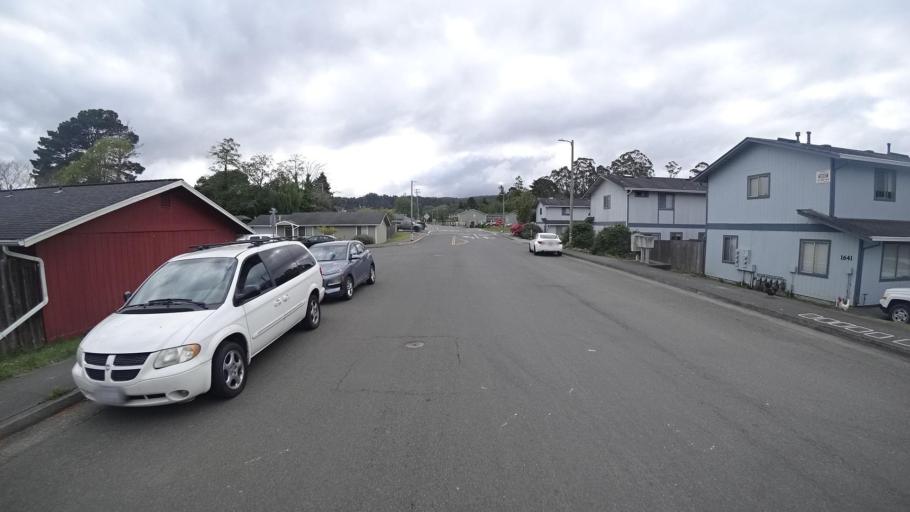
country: US
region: California
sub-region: Humboldt County
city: Arcata
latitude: 40.8793
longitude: -124.0928
